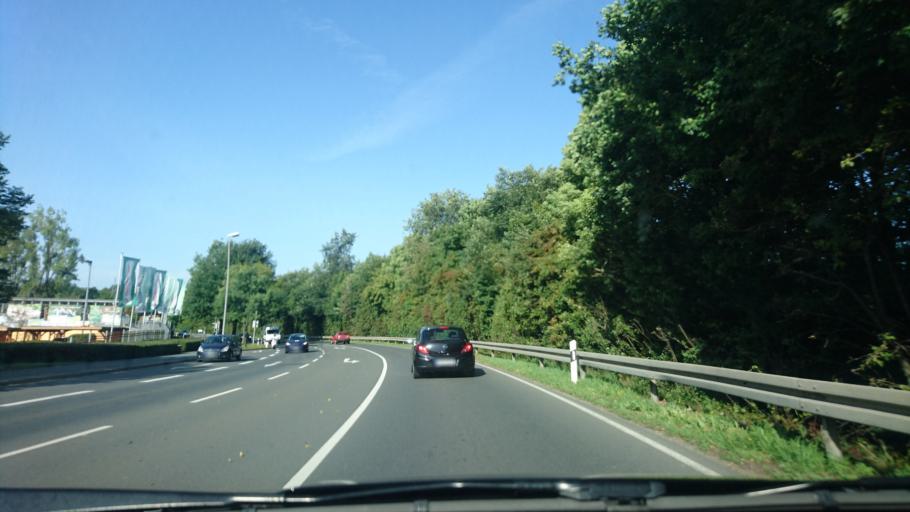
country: DE
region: Bavaria
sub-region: Upper Franconia
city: Bayreuth
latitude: 49.9532
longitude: 11.5671
